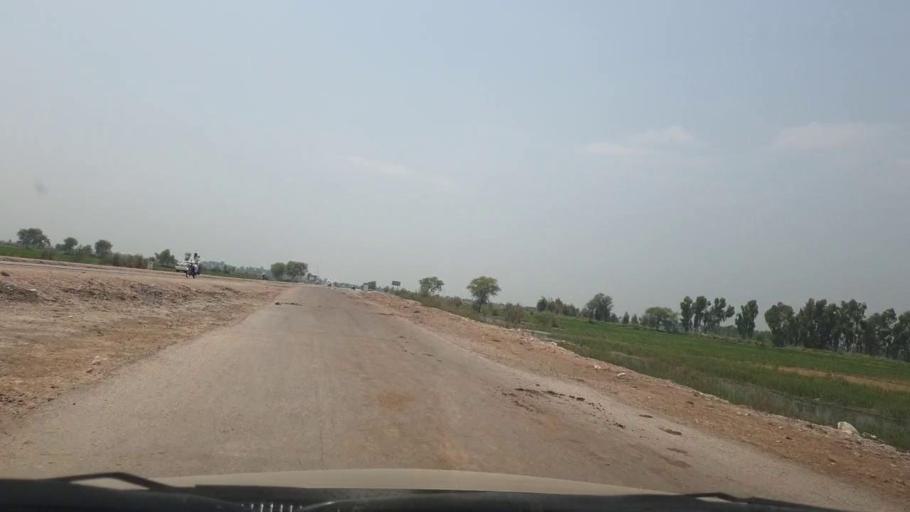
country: PK
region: Sindh
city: Ratodero
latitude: 27.7146
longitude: 68.2769
